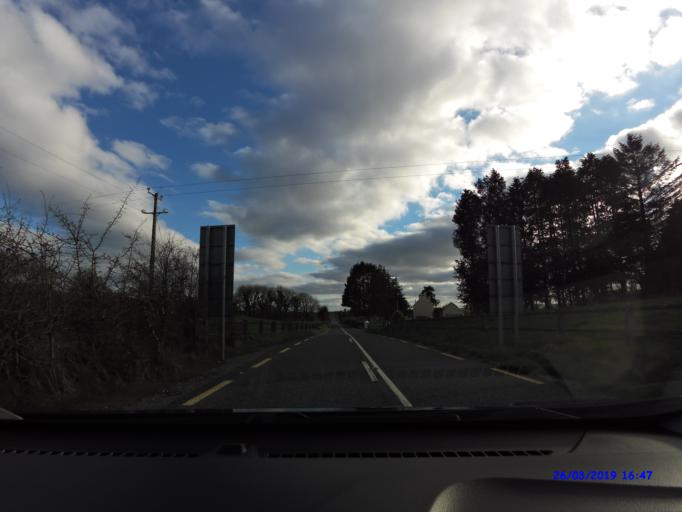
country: IE
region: Connaught
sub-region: Maigh Eo
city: Ballyhaunis
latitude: 53.8139
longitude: -8.7648
